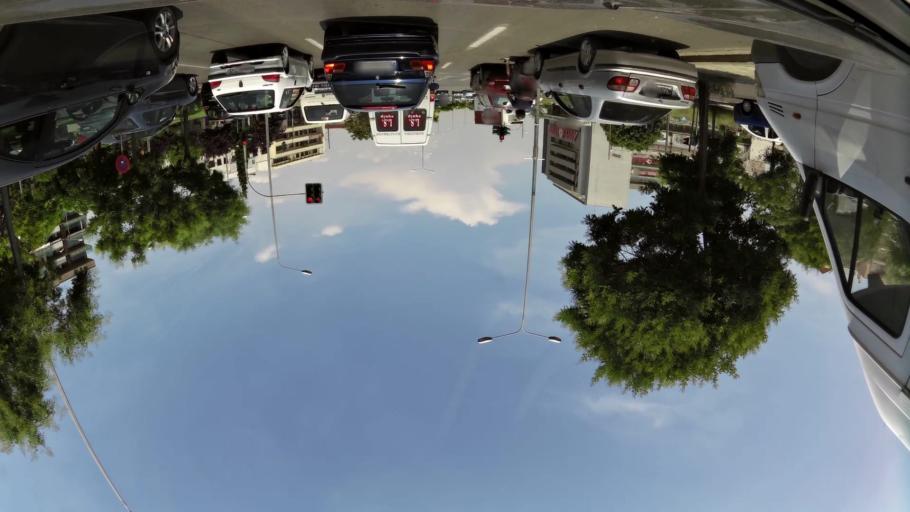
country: GR
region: Central Macedonia
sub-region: Nomos Thessalonikis
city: Ampelokipoi
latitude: 40.6451
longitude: 22.9191
